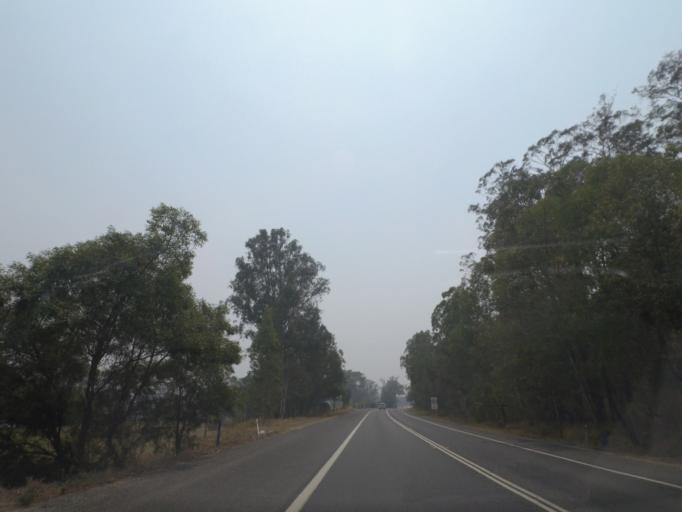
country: AU
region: New South Wales
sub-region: Clarence Valley
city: Maclean
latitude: -29.5544
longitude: 153.1525
